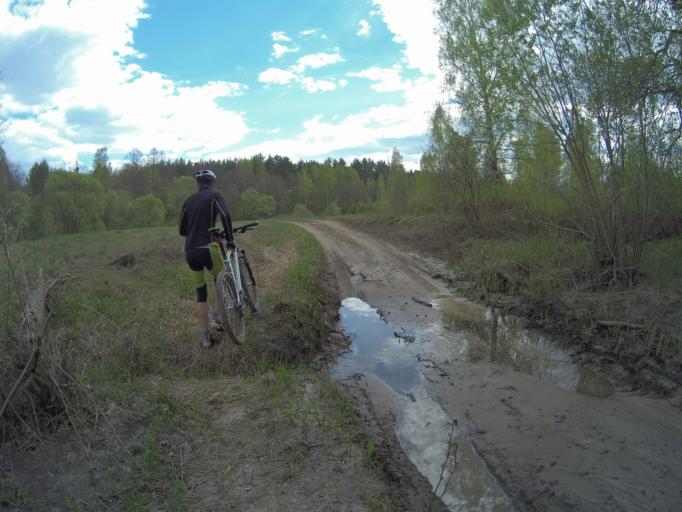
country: RU
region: Vladimir
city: Orgtrud
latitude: 56.1239
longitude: 40.6510
